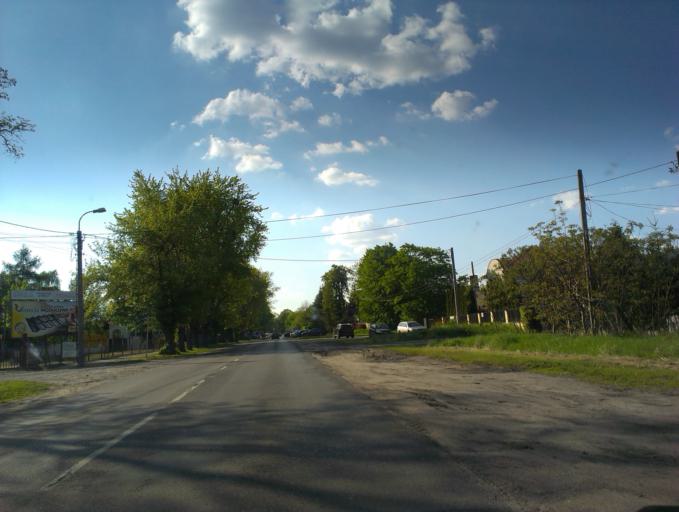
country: PL
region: Masovian Voivodeship
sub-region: Powiat piaseczynski
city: Zabieniec
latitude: 52.0654
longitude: 21.0330
